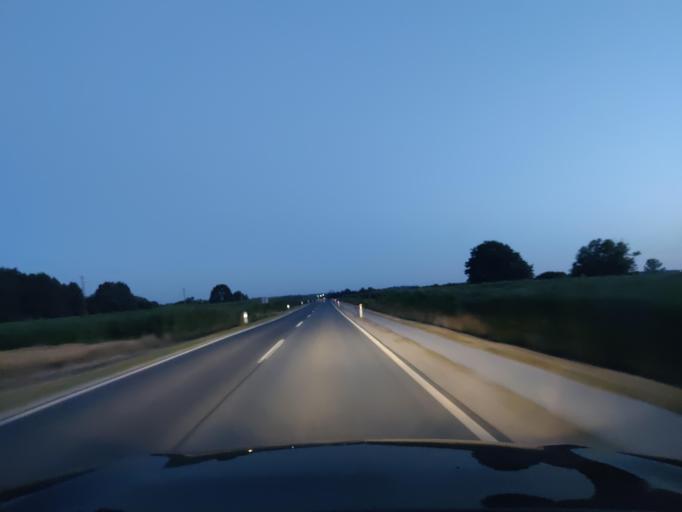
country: HR
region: Medimurska
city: Vratisinec
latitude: 46.5017
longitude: 16.4306
